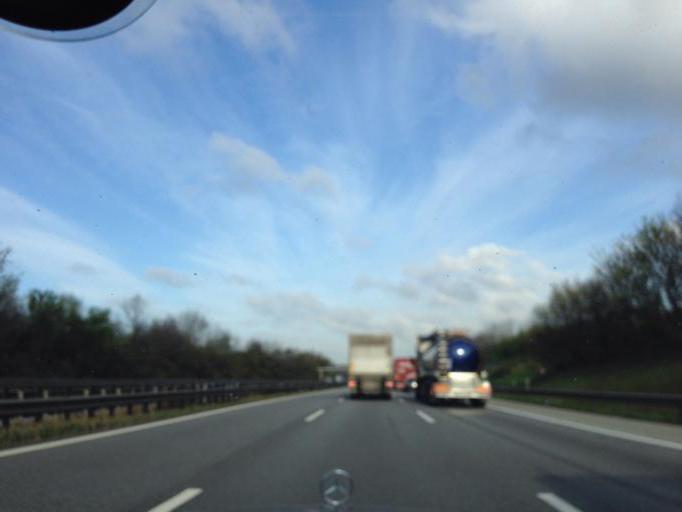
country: DE
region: Hamburg
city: Rothenburgsort
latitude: 53.5077
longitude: 10.0763
